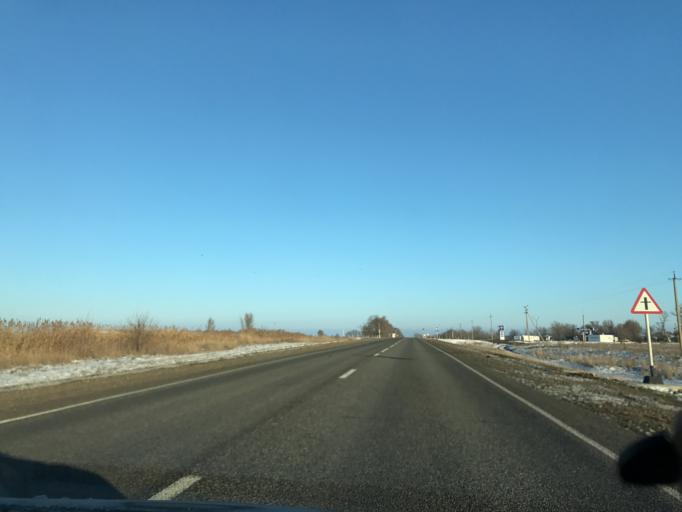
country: RU
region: Stavropol'skiy
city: Bezopasnoye
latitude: 45.5865
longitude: 41.9455
